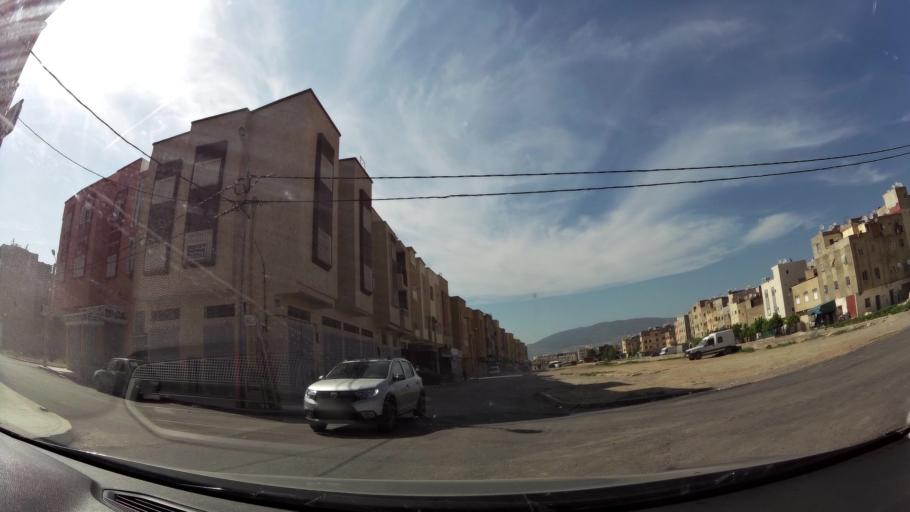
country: MA
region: Fes-Boulemane
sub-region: Fes
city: Fes
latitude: 34.0133
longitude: -5.0355
